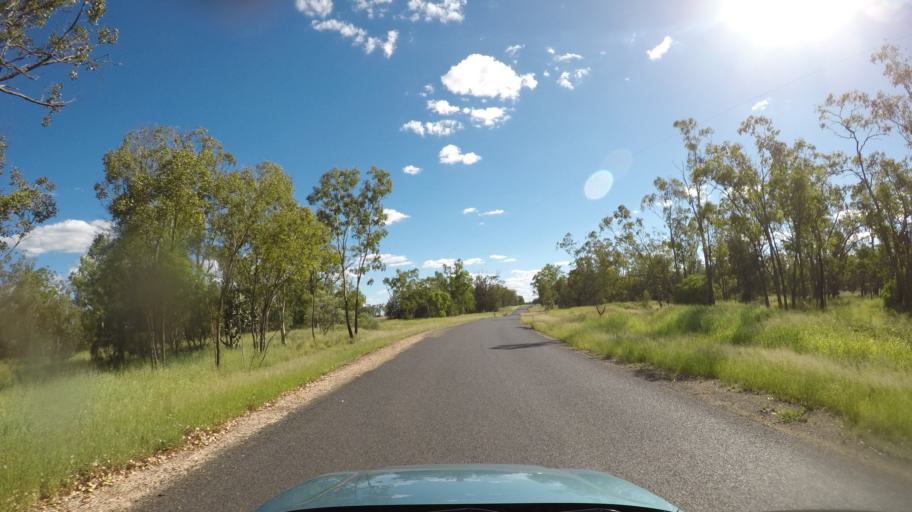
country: AU
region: Queensland
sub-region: Goondiwindi
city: Goondiwindi
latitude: -28.1741
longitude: 150.4704
